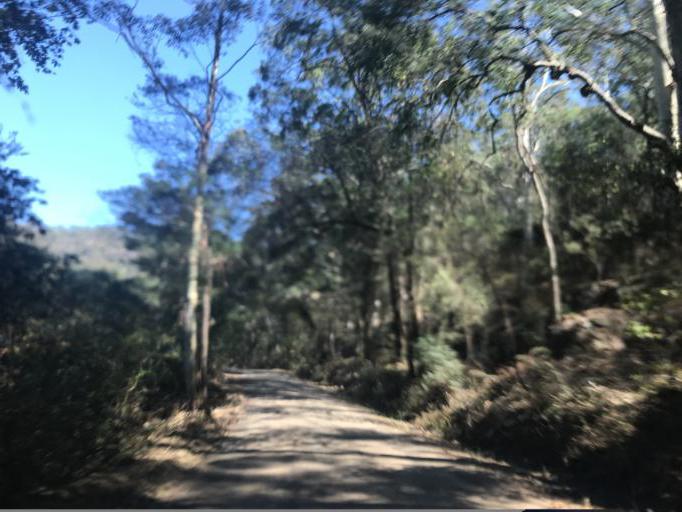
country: AU
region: New South Wales
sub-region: Wyong Shire
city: Little Jilliby
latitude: -33.1972
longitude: 151.0247
